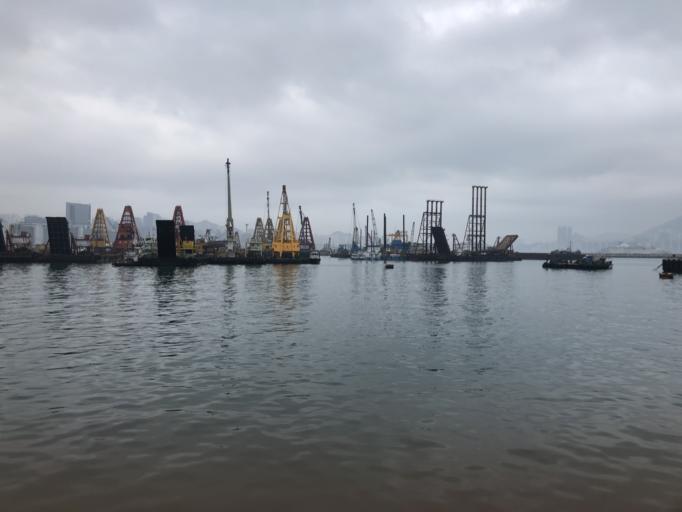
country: HK
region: Kowloon City
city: Kowloon
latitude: 22.3158
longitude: 114.1943
